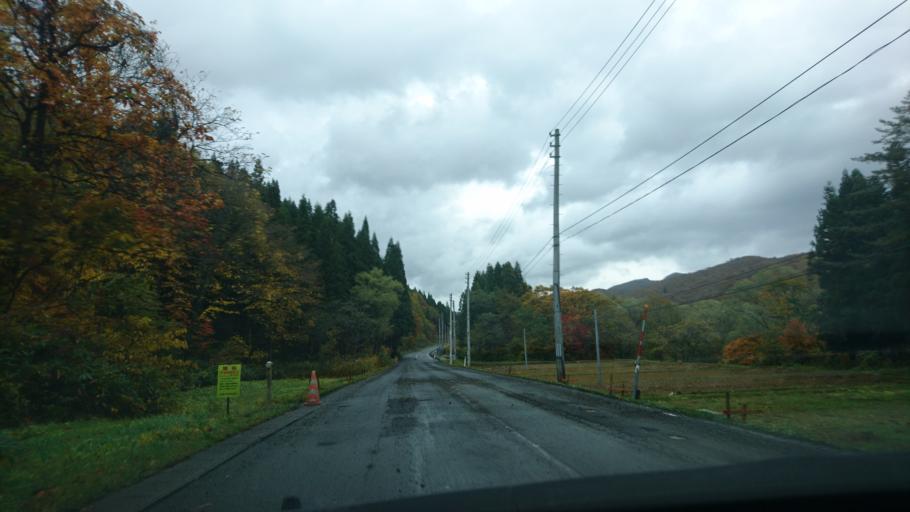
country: JP
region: Iwate
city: Shizukuishi
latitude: 39.5009
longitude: 140.8179
